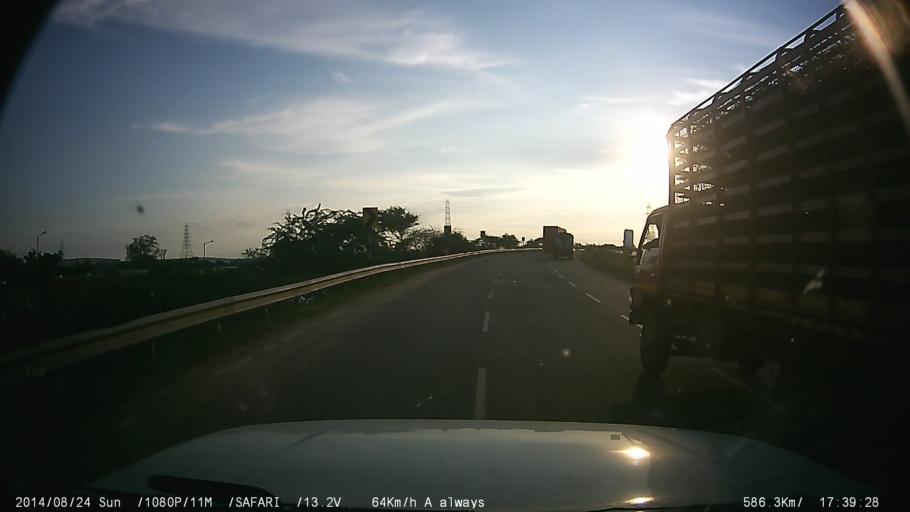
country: IN
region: Tamil Nadu
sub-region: Kancheepuram
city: Sriperumbudur
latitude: 12.9209
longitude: 79.8813
